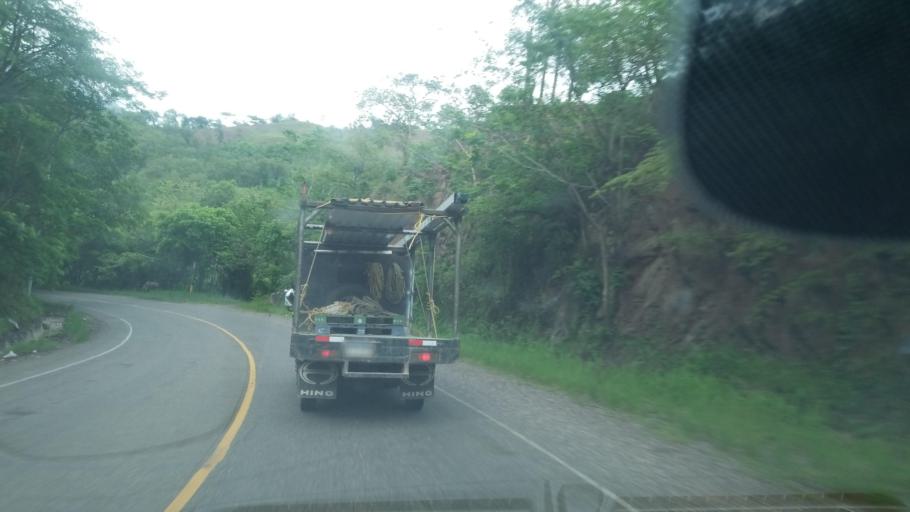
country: HN
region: Santa Barbara
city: Ceguaca
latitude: 14.8083
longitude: -88.1864
